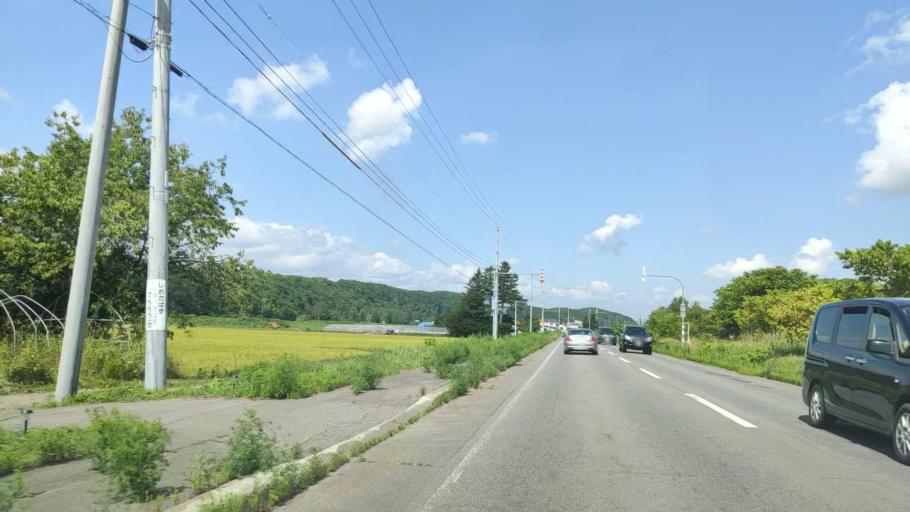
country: JP
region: Hokkaido
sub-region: Asahikawa-shi
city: Asahikawa
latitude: 43.6305
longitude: 142.4612
